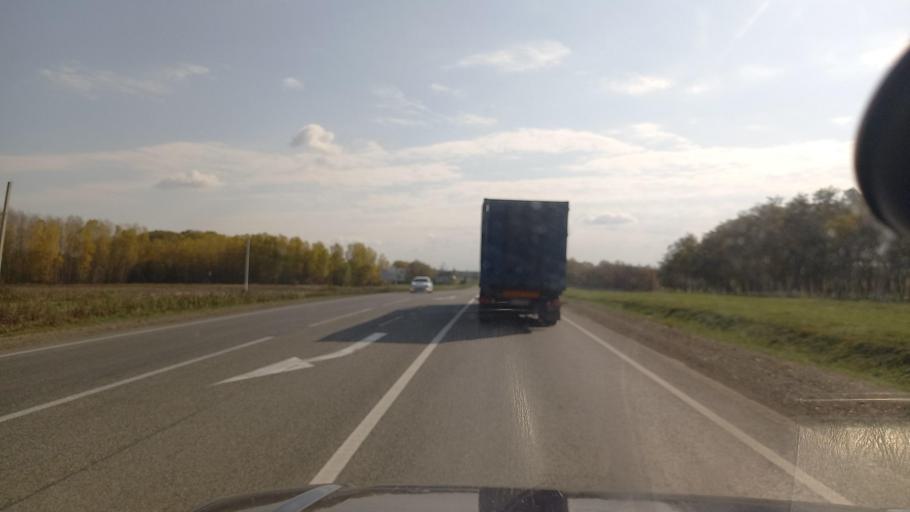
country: RU
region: Krasnodarskiy
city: Novoukrainskiy
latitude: 44.8873
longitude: 38.0806
